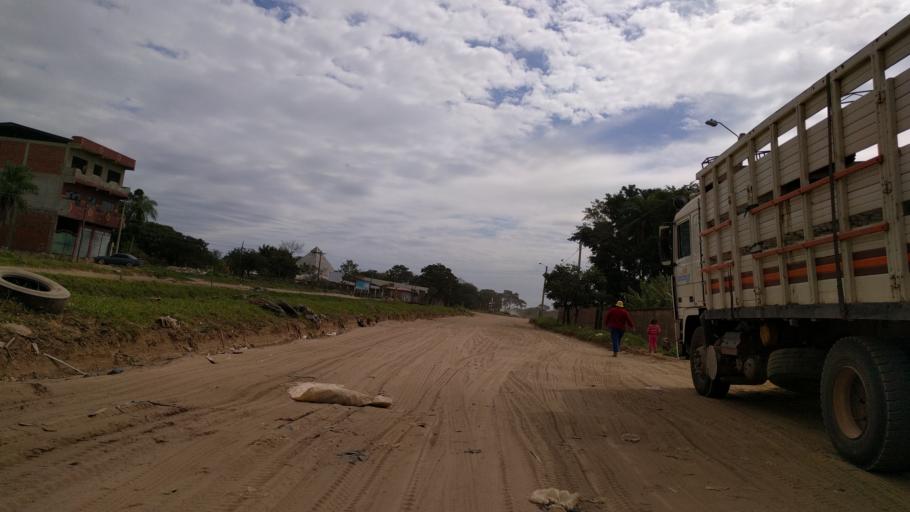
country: BO
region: Santa Cruz
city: Santa Cruz de la Sierra
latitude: -17.8246
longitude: -63.2455
